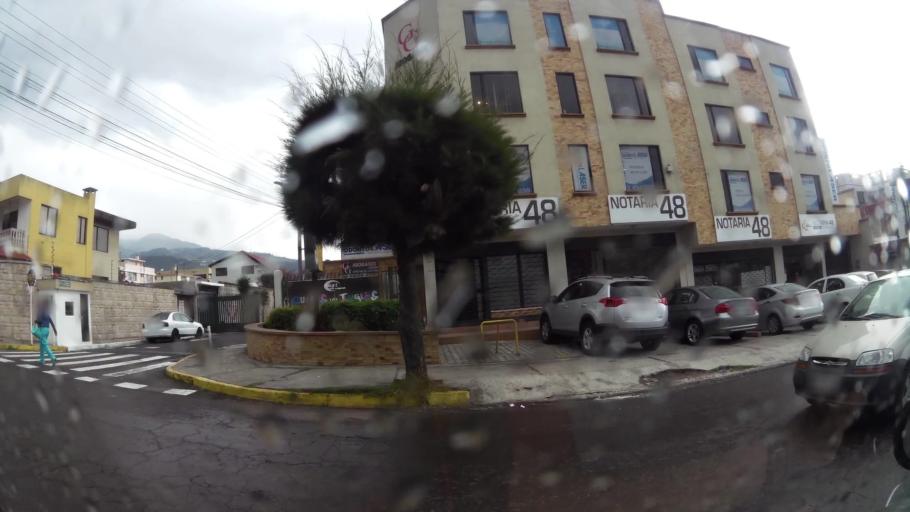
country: EC
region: Pichincha
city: Quito
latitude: -0.1060
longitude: -78.4907
